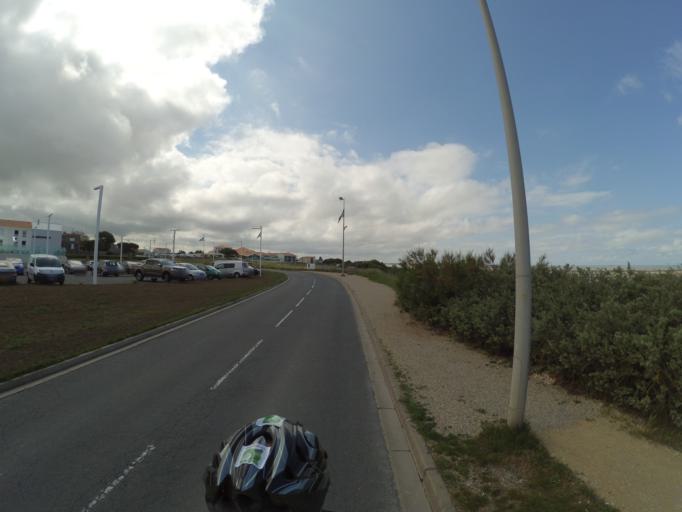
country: FR
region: Poitou-Charentes
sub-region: Departement de la Charente-Maritime
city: Chatelaillon-Plage
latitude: 46.0598
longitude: -1.0898
